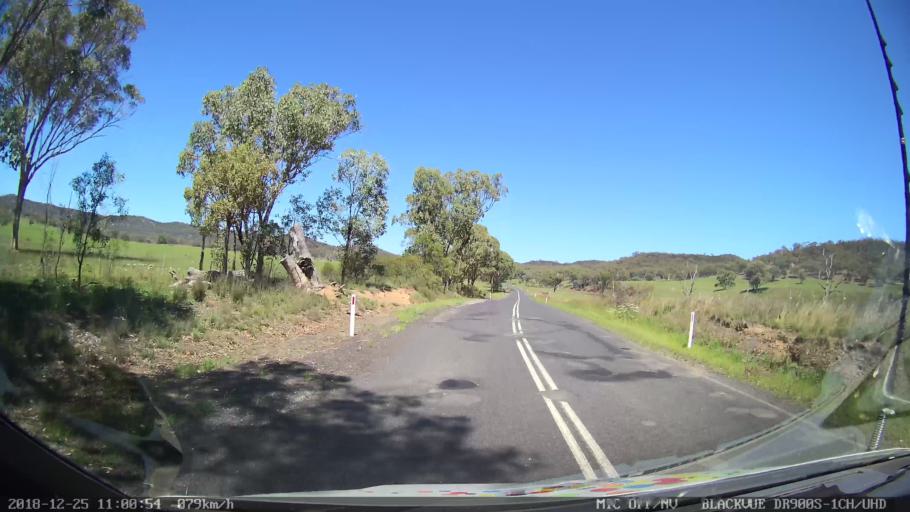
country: AU
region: New South Wales
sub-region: Upper Hunter Shire
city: Merriwa
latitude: -32.4030
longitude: 150.2089
